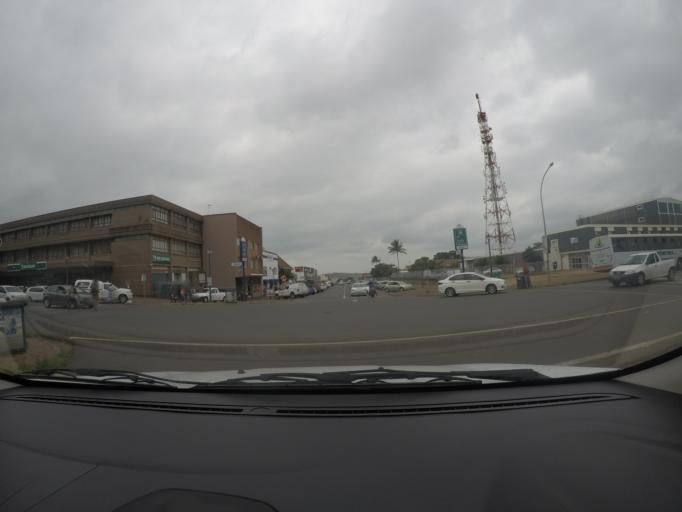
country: ZA
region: KwaZulu-Natal
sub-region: uThungulu District Municipality
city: Empangeni
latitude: -28.7442
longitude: 31.8906
